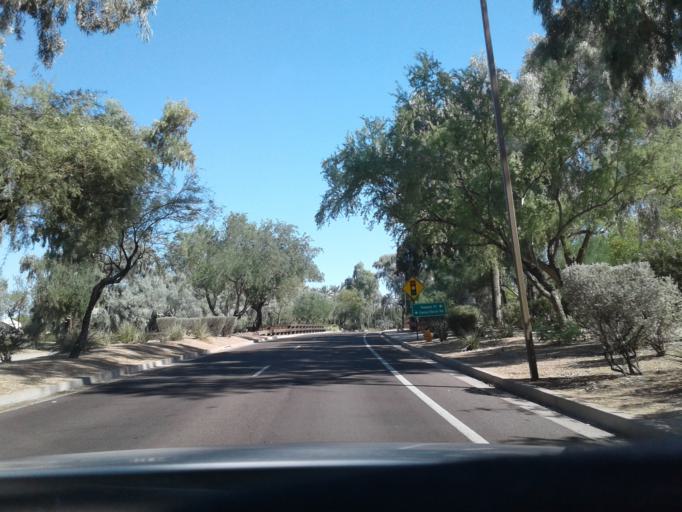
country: US
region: Arizona
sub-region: Maricopa County
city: Paradise Valley
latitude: 33.5638
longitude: -111.9127
